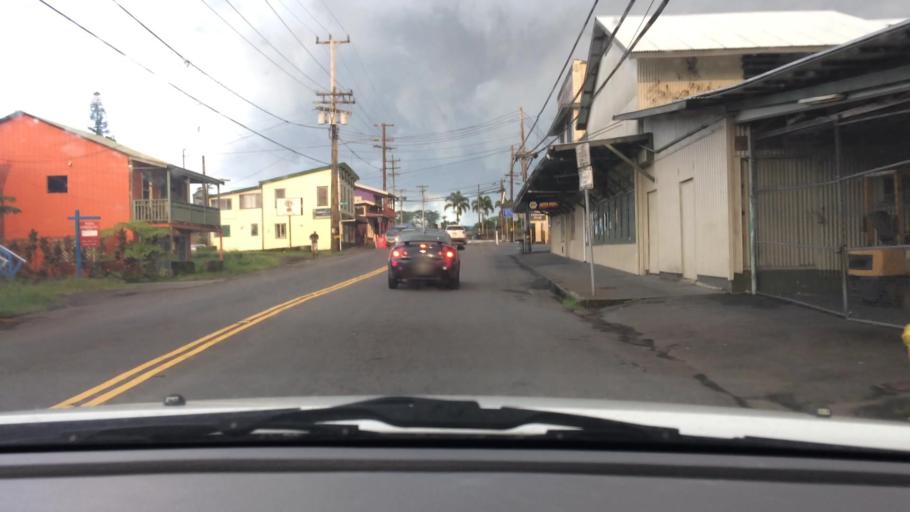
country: US
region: Hawaii
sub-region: Hawaii County
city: Hawaiian Paradise Park
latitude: 19.4943
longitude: -154.9473
